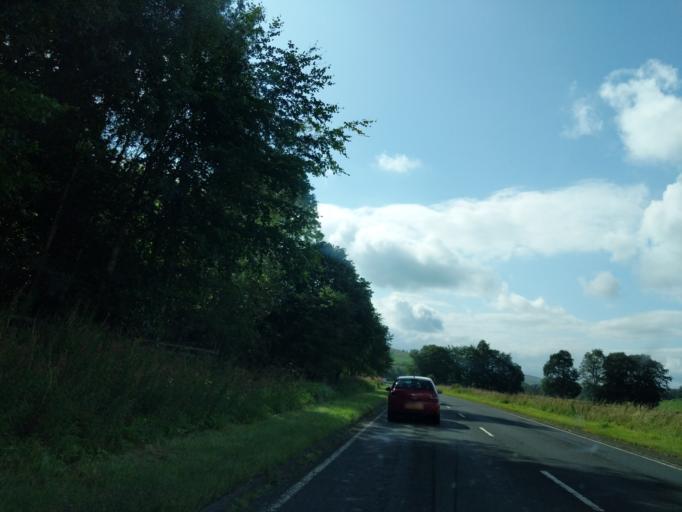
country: GB
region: Scotland
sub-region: The Scottish Borders
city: Peebles
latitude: 55.7235
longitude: -3.2052
